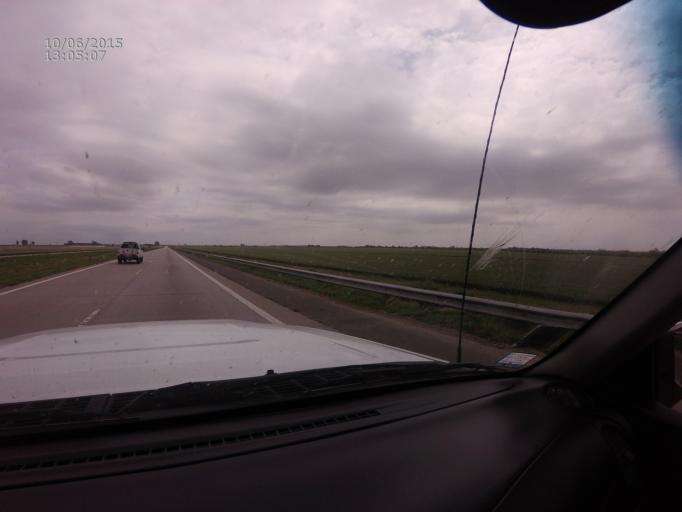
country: AR
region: Cordoba
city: General Roca
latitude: -32.7760
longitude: -61.7995
